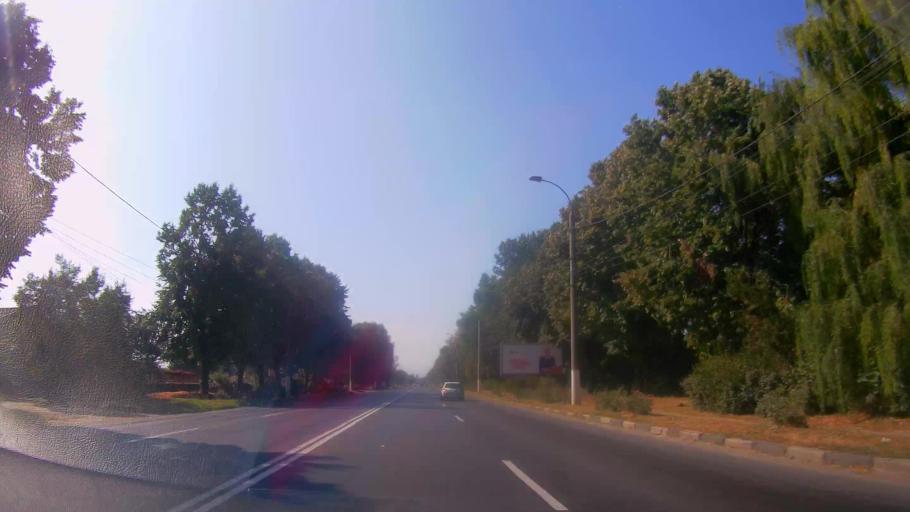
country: RO
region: Giurgiu
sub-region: Comuna Fratesti
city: Remus
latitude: 43.9255
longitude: 25.9745
